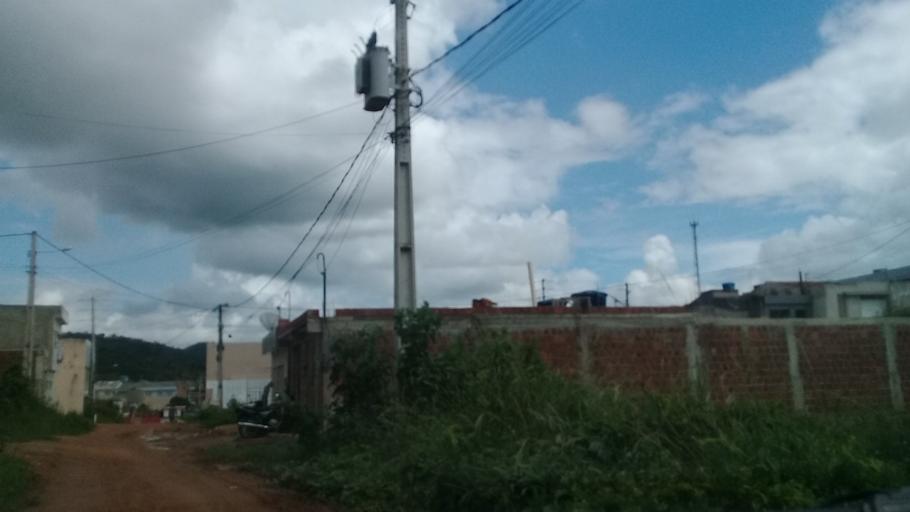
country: BR
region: Pernambuco
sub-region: Vitoria De Santo Antao
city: Vitoria de Santo Antao
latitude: -8.1316
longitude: -35.2920
